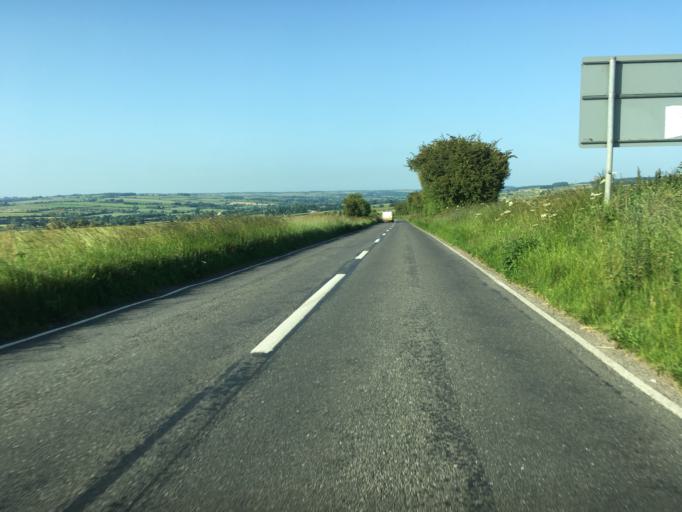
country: GB
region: England
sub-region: Oxfordshire
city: Shipton under Wychwood
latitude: 51.8424
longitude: -1.5898
